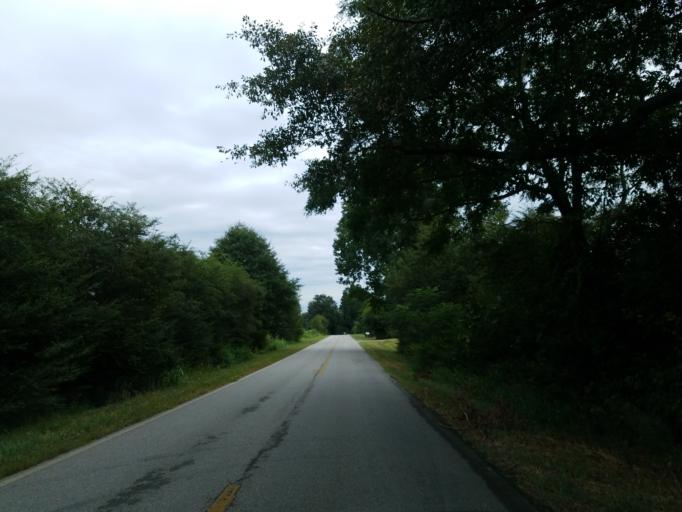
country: US
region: Georgia
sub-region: Lamar County
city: Barnesville
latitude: 33.0041
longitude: -84.0656
